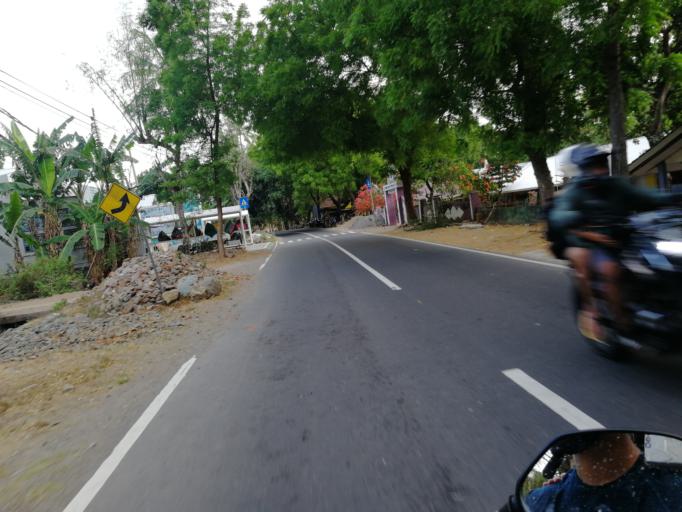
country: ID
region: West Nusa Tenggara
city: Karangsubagan
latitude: -8.4532
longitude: 116.0399
